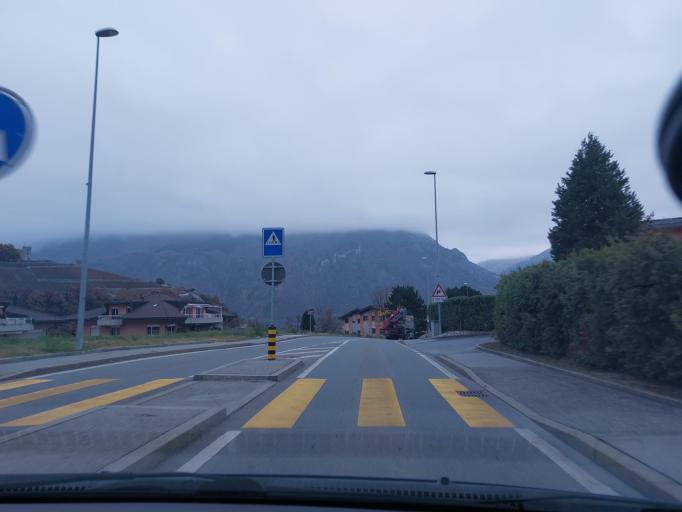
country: CH
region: Valais
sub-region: Sierre District
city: Veyras
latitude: 46.3029
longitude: 7.5402
